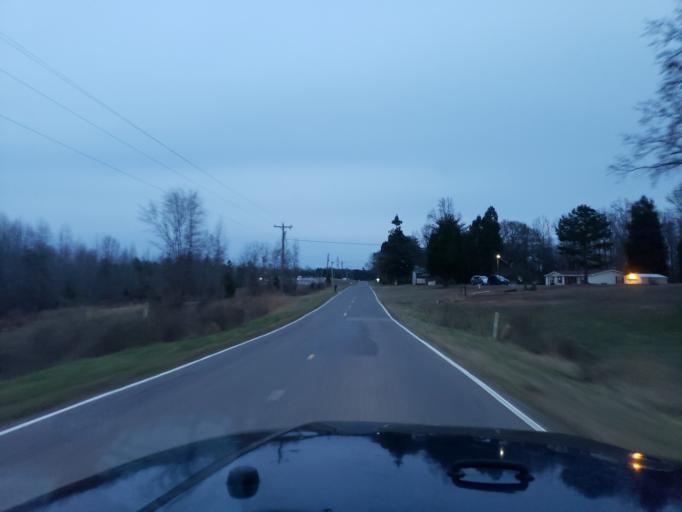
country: US
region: North Carolina
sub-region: Cleveland County
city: White Plains
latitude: 35.1753
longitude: -81.4120
